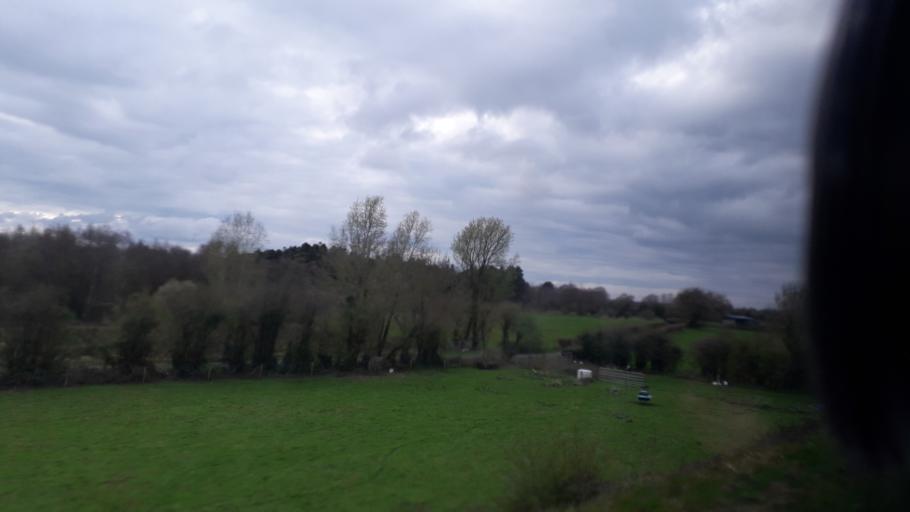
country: IE
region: Leinster
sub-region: An Iarmhi
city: Castlepollard
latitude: 53.6441
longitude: -7.4222
